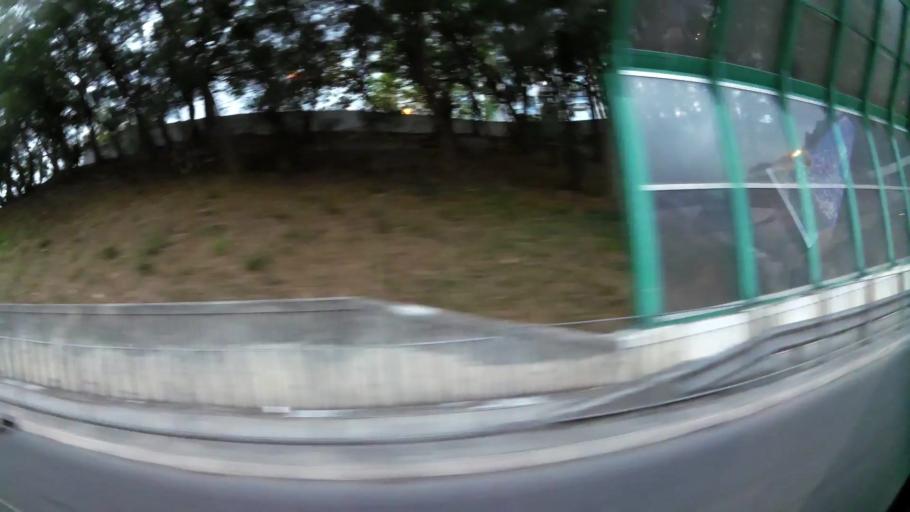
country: HK
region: Tsuen Wan
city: Tsuen Wan
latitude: 22.3530
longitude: 114.0985
